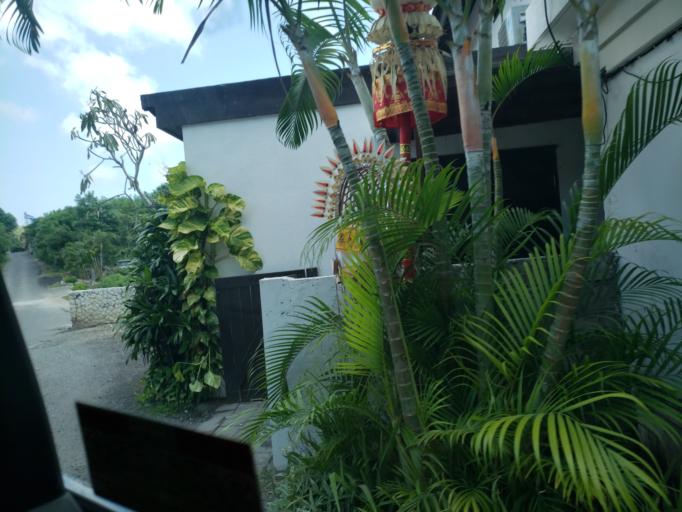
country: ID
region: Bali
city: Kangin
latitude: -8.8459
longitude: 115.1485
